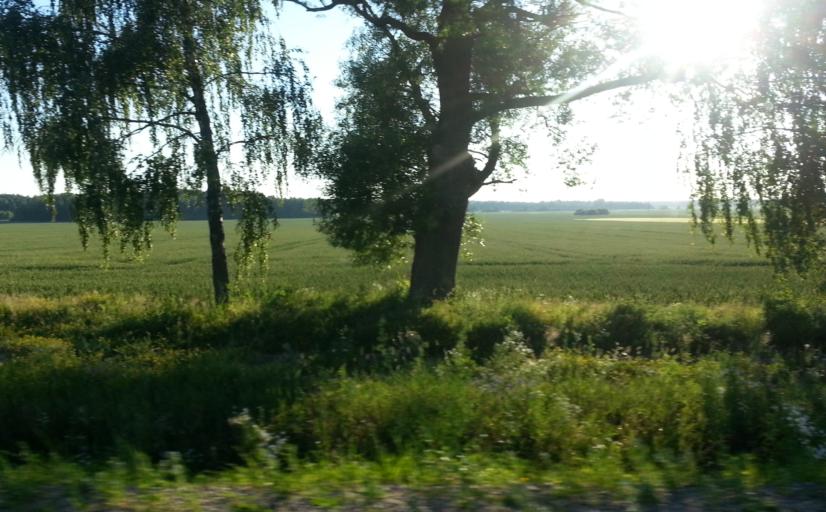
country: LT
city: Ramygala
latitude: 55.6090
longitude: 24.3477
